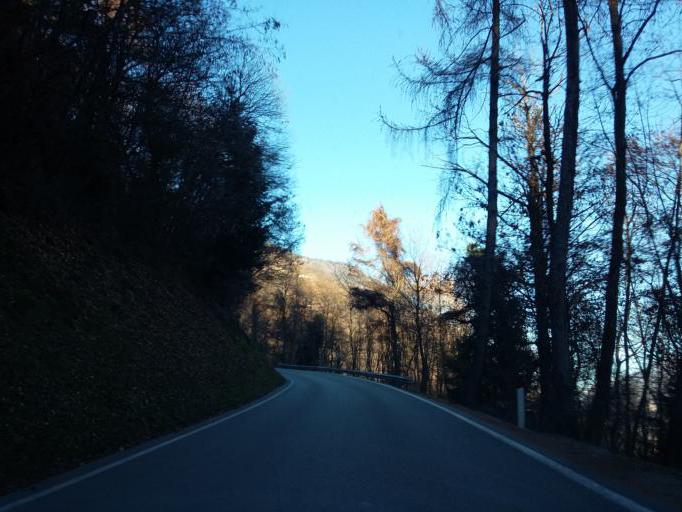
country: IT
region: Trentino-Alto Adige
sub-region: Provincia di Trento
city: Brione
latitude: 45.8958
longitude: 10.6009
